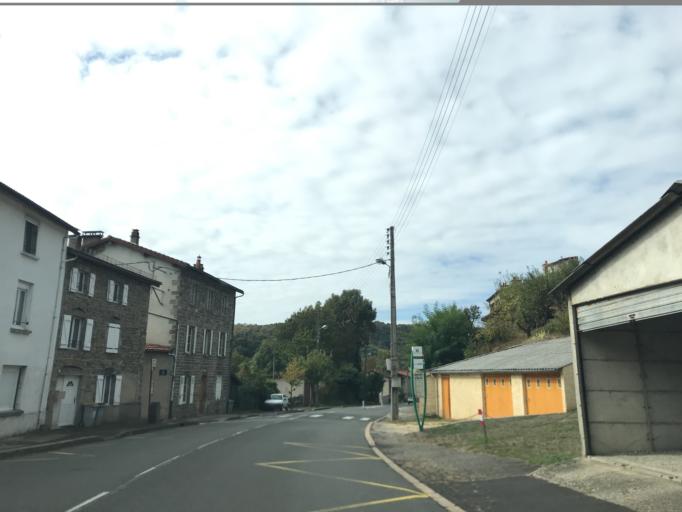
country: FR
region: Auvergne
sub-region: Departement du Puy-de-Dome
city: La Monnerie-le-Montel
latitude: 45.8653
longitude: 3.5843
